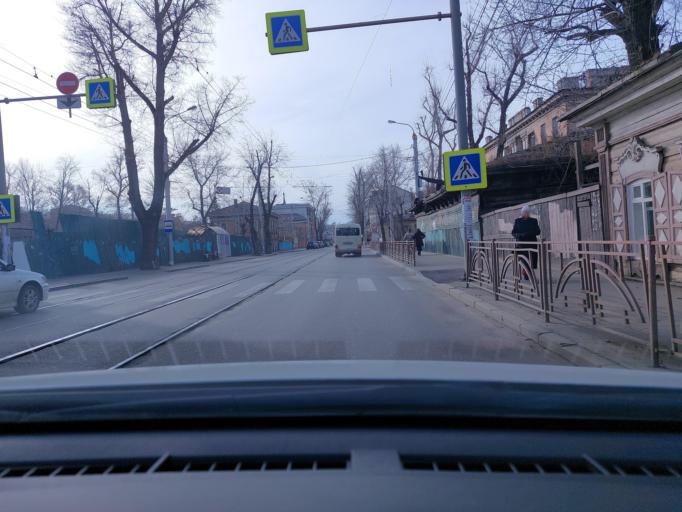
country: RU
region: Irkutsk
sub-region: Irkutskiy Rayon
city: Irkutsk
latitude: 52.2792
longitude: 104.2926
